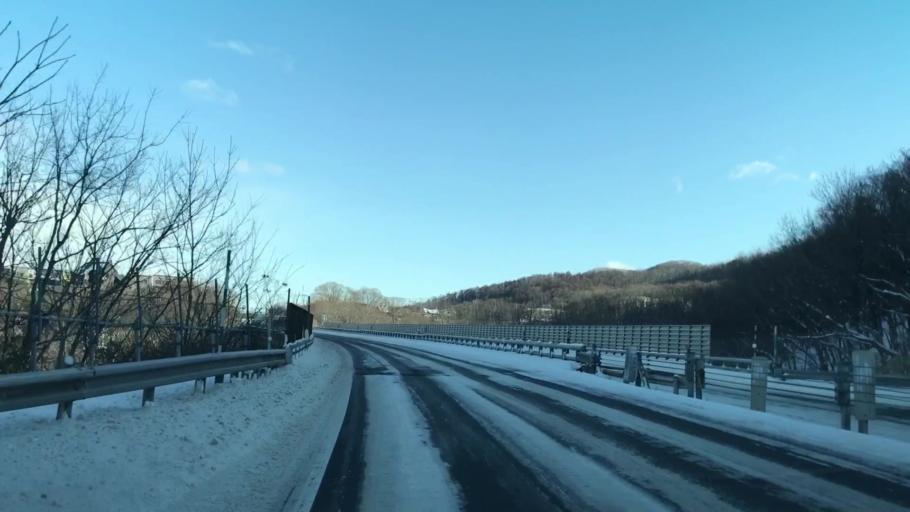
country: JP
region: Hokkaido
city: Sapporo
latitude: 43.1264
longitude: 141.1978
